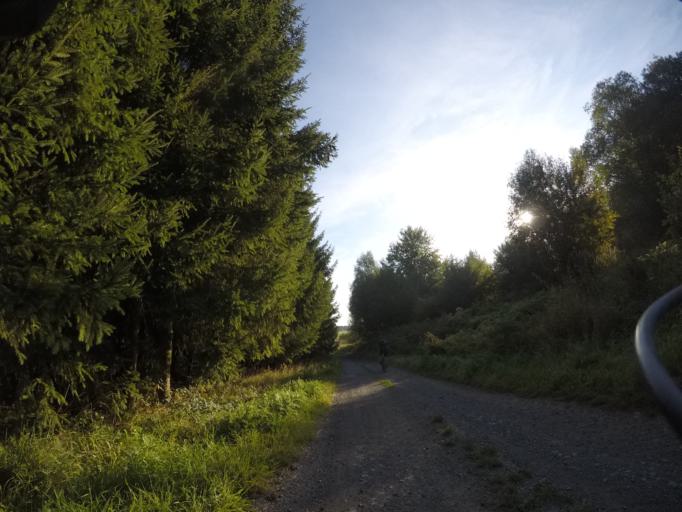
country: BE
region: Wallonia
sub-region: Province du Luxembourg
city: Bastogne
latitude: 49.9581
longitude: 5.7059
